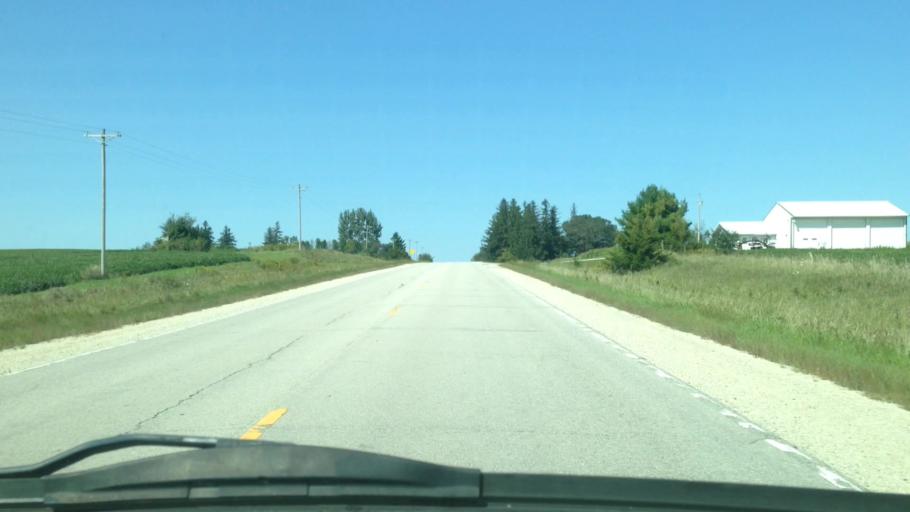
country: US
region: Minnesota
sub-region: Houston County
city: Spring Grove
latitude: 43.6176
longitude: -91.7903
